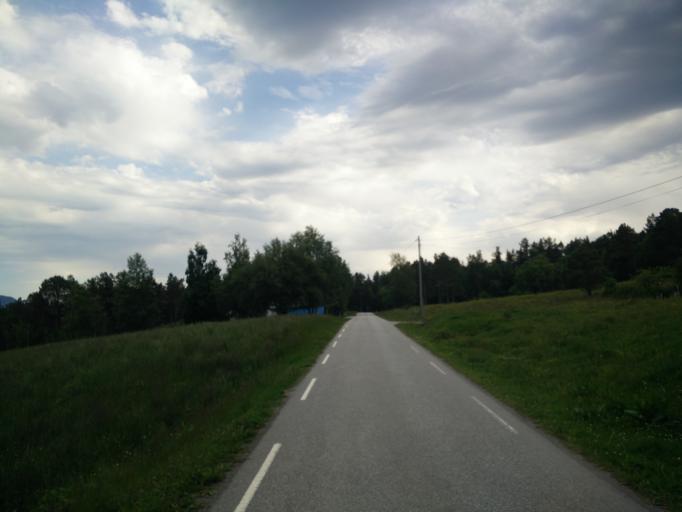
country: NO
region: More og Romsdal
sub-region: Kristiansund
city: Rensvik
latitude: 63.0359
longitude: 7.9548
